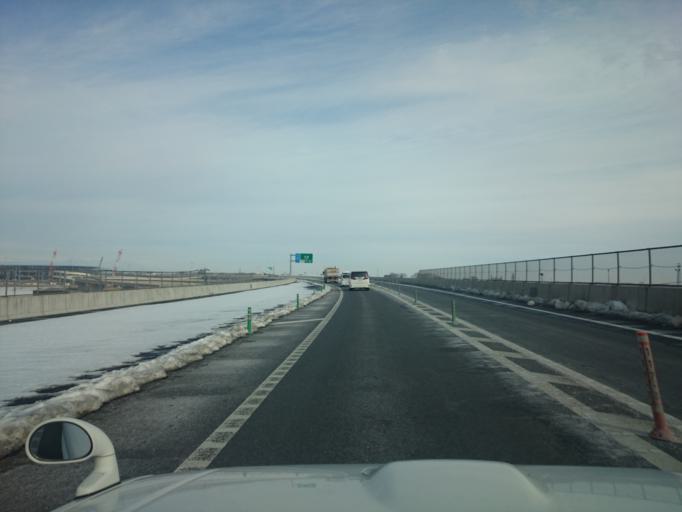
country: JP
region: Ibaraki
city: Sakai
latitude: 36.0906
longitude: 139.7617
